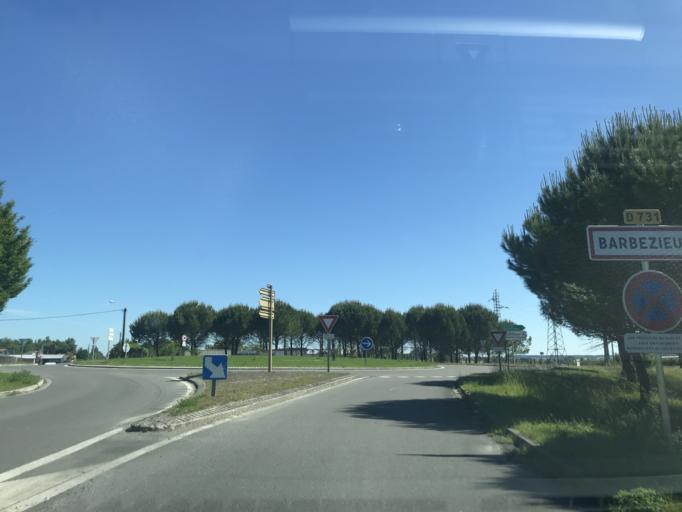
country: FR
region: Poitou-Charentes
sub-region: Departement de la Charente
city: Barbezieux-Saint-Hilaire
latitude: 45.4589
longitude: -0.1523
